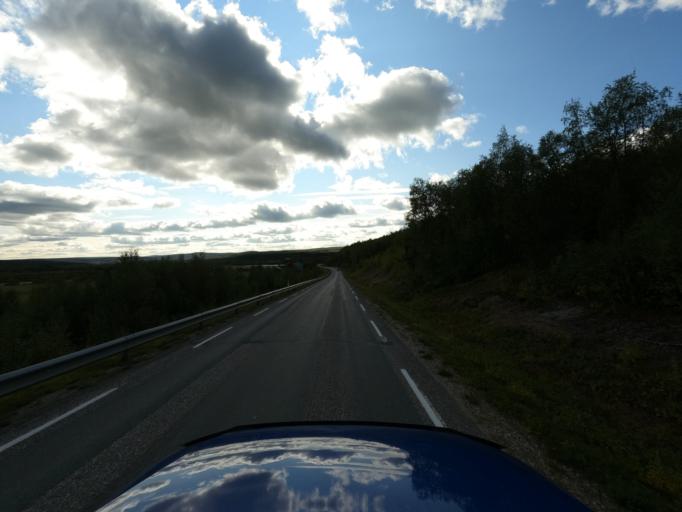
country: NO
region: Finnmark Fylke
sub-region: Karasjok
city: Karasjohka
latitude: 69.4270
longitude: 25.7940
